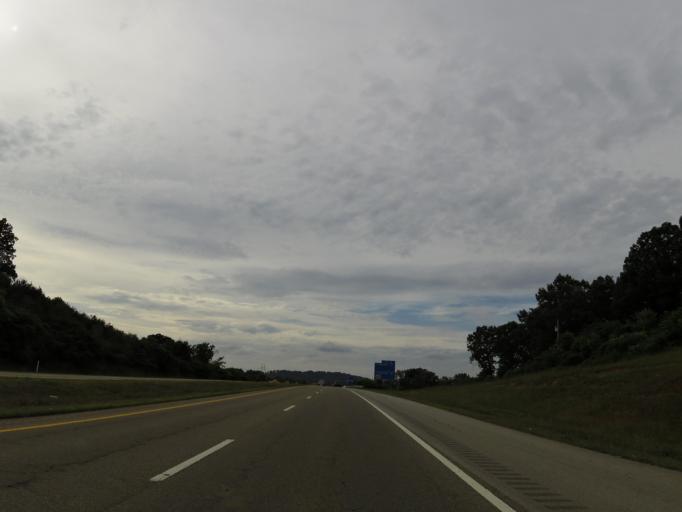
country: US
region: Tennessee
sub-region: Blount County
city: Eagleton Village
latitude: 35.8172
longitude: -83.9500
